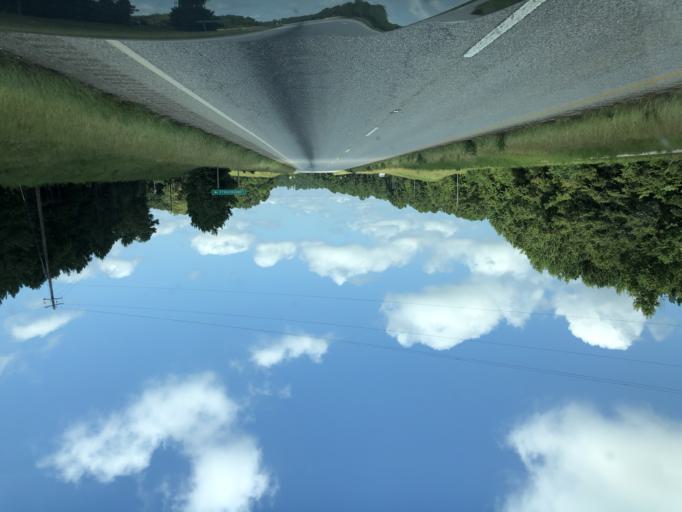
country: US
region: Alabama
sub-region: Henry County
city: Abbeville
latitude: 31.6355
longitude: -85.2800
